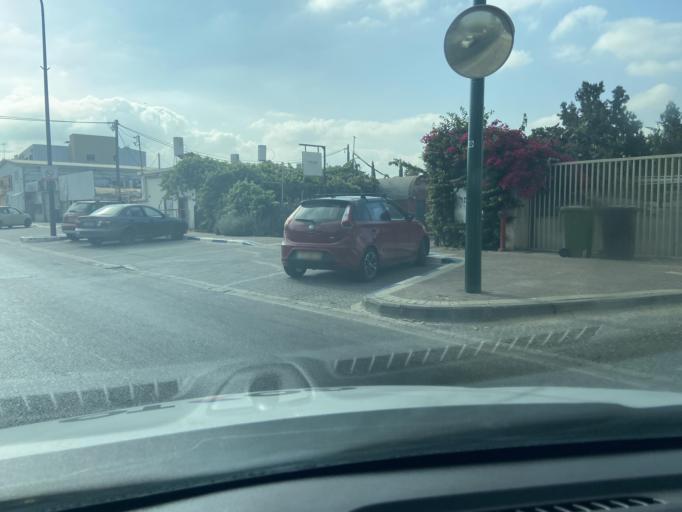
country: IL
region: Central District
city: Yehud
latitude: 32.0281
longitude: 34.8846
